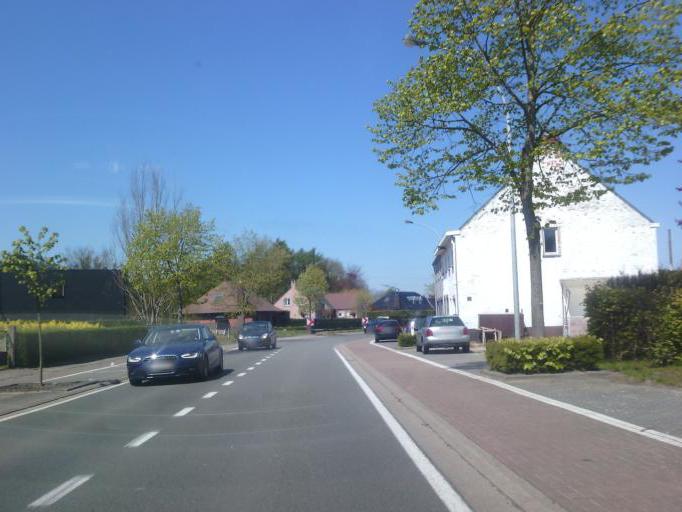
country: BE
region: Flanders
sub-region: Provincie Oost-Vlaanderen
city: Waasmunster
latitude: 51.1314
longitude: 4.0786
